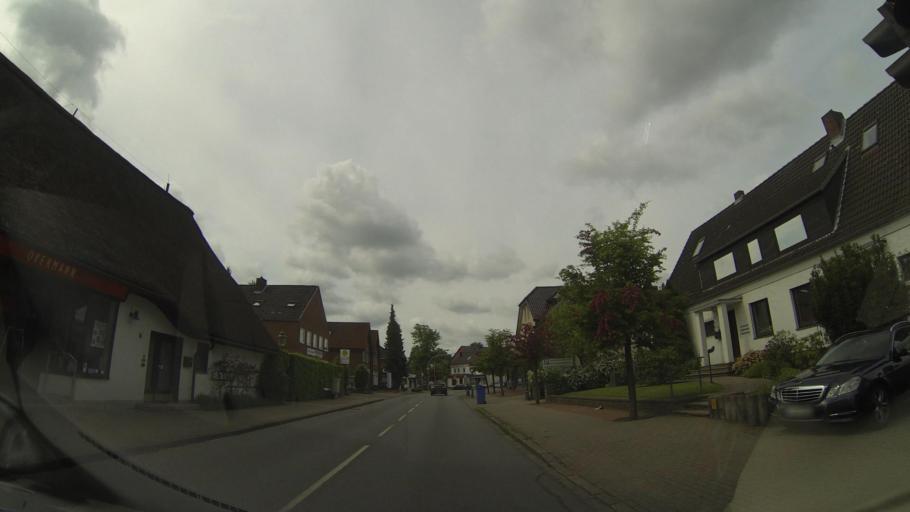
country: DE
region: Schleswig-Holstein
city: Rellingen
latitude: 53.6537
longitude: 9.8302
